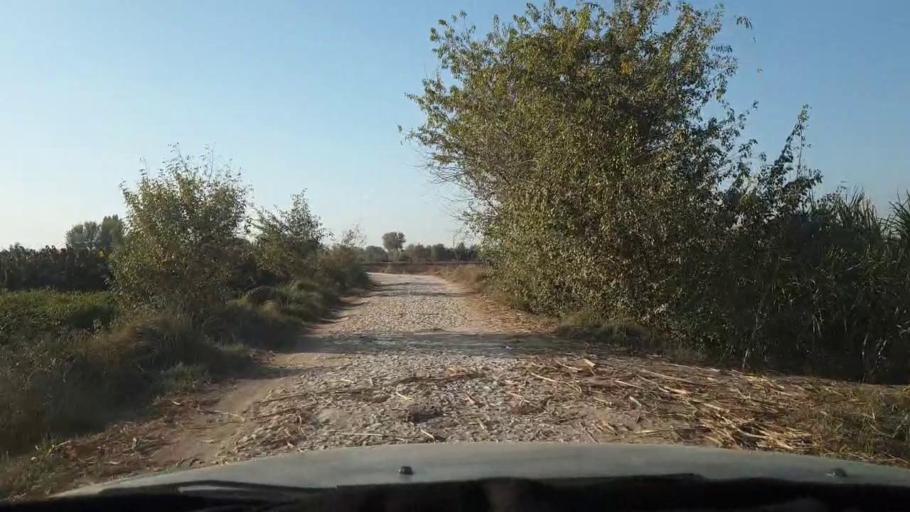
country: PK
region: Sindh
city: Adilpur
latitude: 27.9521
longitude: 69.2325
